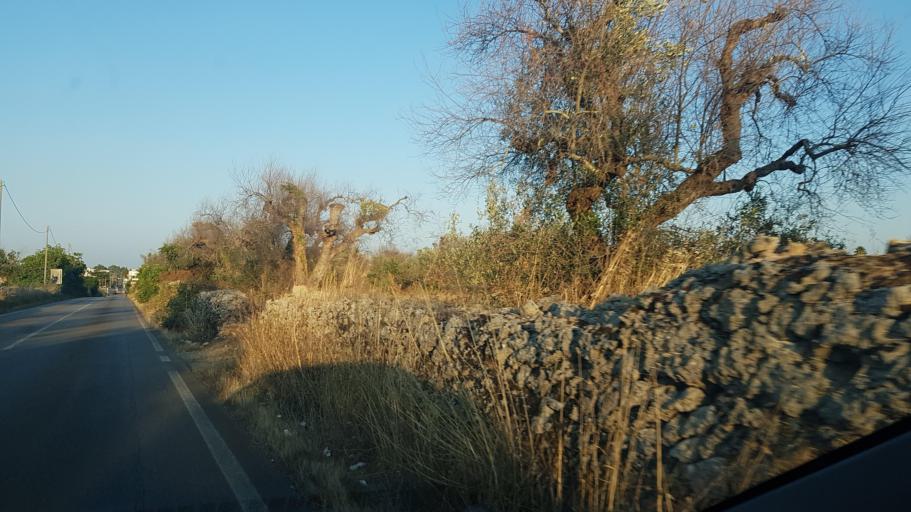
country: IT
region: Apulia
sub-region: Provincia di Lecce
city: Lucugnano
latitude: 39.9382
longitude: 18.3148
